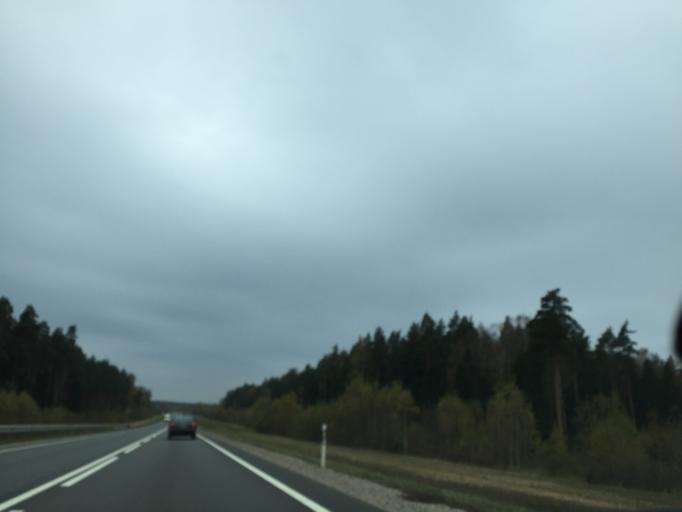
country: LV
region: Ozolnieku
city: Ozolnieki
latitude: 56.7010
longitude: 23.8315
